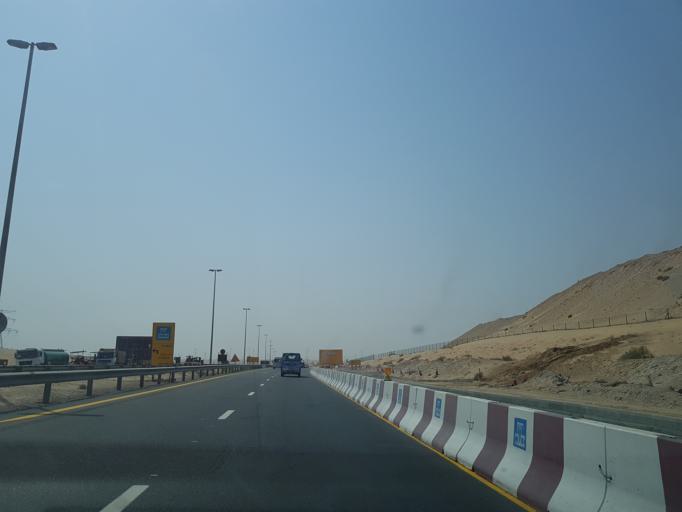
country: AE
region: Ash Shariqah
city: Sharjah
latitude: 25.1421
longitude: 55.4238
